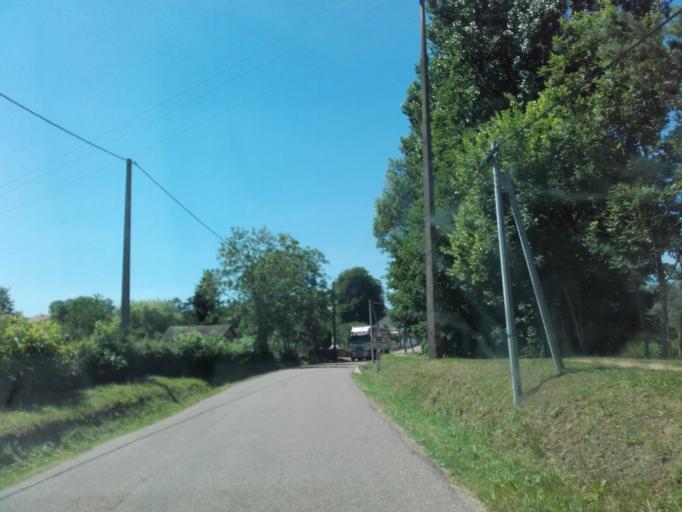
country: FR
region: Bourgogne
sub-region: Departement de Saone-et-Loire
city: Saint-Leger-sur-Dheune
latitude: 46.8917
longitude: 4.6783
